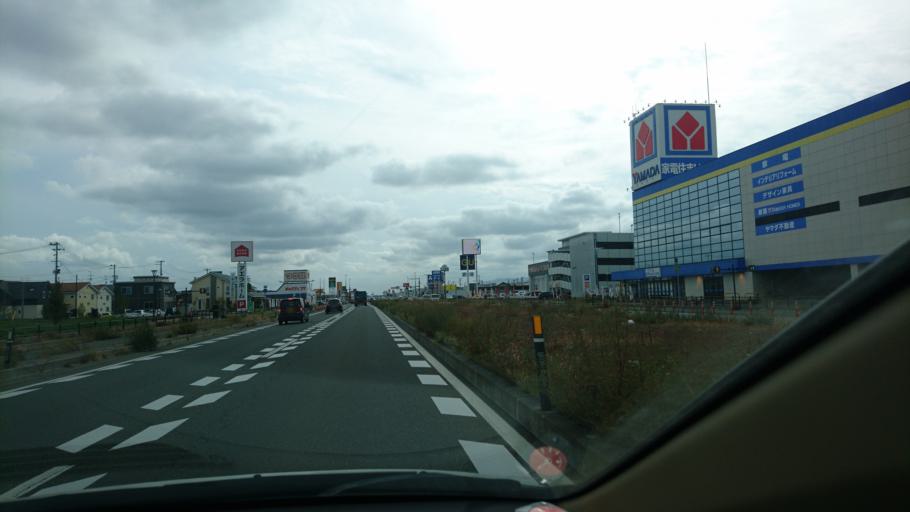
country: JP
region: Iwate
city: Morioka-shi
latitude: 39.6792
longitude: 141.1352
